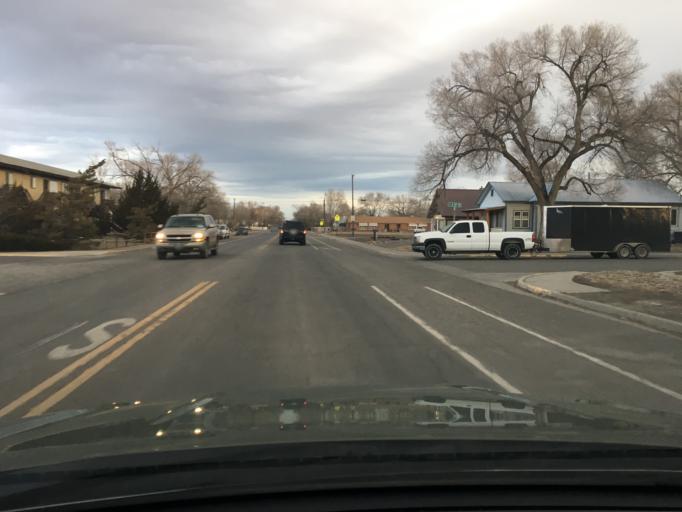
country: US
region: Colorado
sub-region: Montrose County
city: Montrose
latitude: 38.4723
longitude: -107.8650
